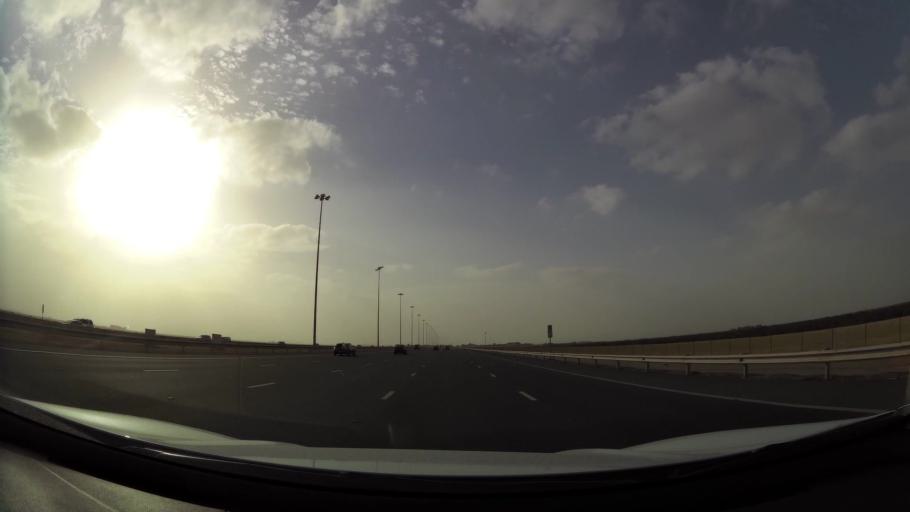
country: AE
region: Abu Dhabi
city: Abu Dhabi
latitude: 24.5250
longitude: 54.5077
